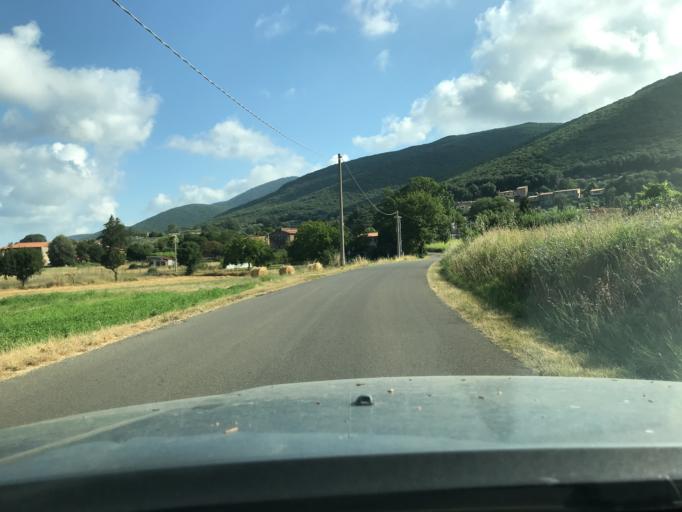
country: IT
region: Umbria
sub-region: Provincia di Terni
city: Guardea
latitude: 42.6272
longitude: 12.3165
